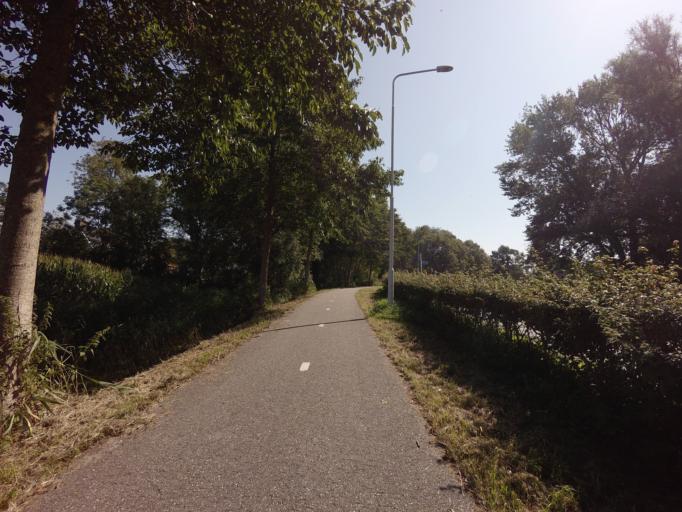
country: NL
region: Friesland
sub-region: Gemeente Dongeradeel
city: Ternaard
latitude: 53.3631
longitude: 5.9788
